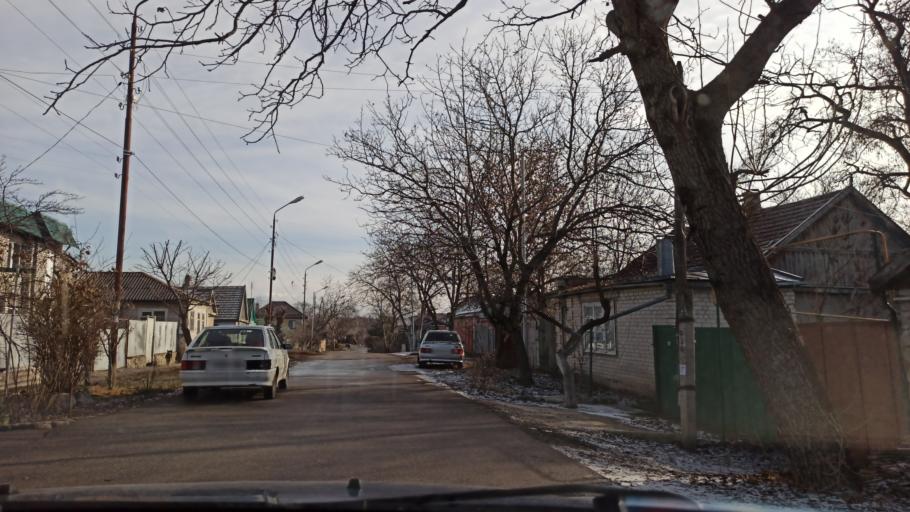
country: RU
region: Stavropol'skiy
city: Yessentukskaya
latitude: 44.0392
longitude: 42.8758
